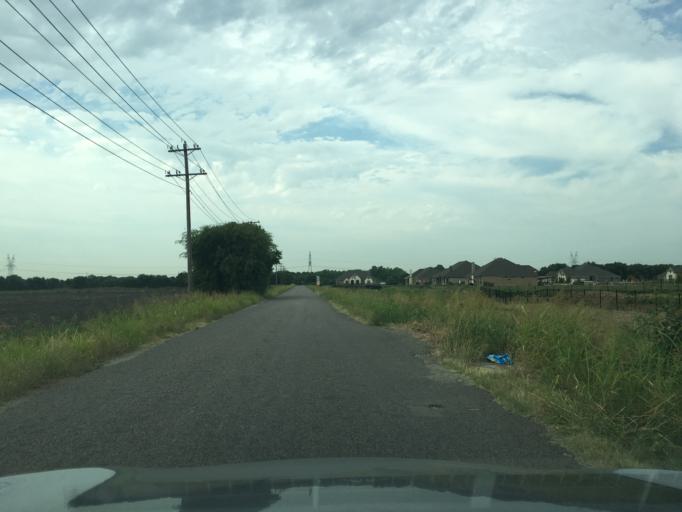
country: US
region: Texas
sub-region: Collin County
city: Parker
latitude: 33.0666
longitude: -96.6012
